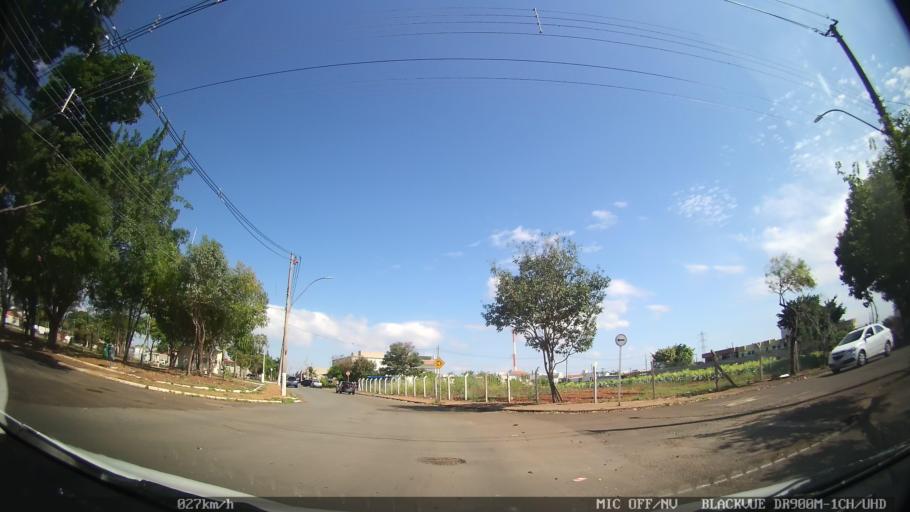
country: BR
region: Sao Paulo
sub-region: Americana
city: Americana
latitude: -22.7200
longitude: -47.3089
